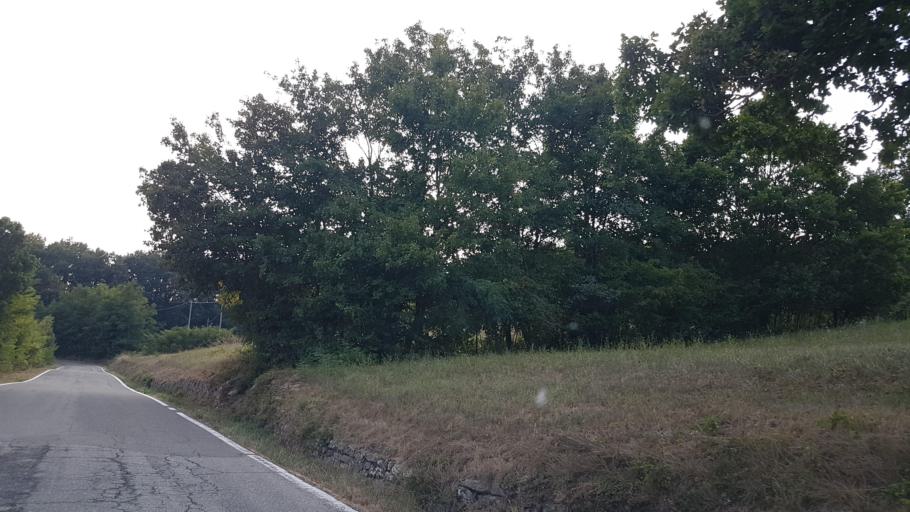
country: IT
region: Emilia-Romagna
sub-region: Provincia di Parma
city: Albareto
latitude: 44.4686
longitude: 9.7068
